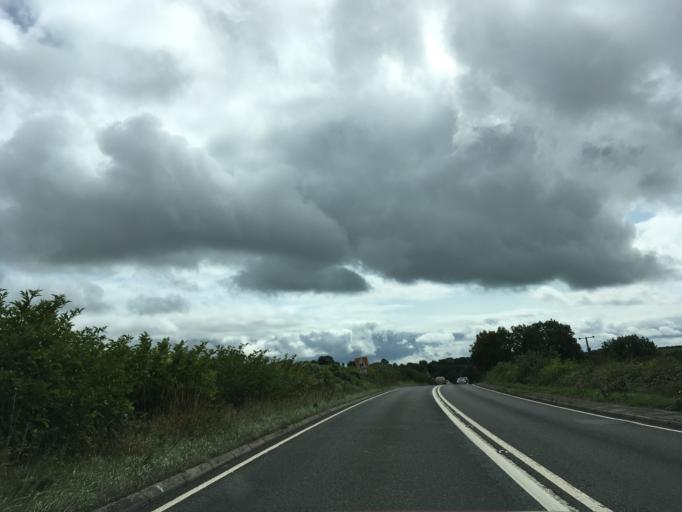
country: GB
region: England
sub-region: South Gloucestershire
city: Cold Ashton
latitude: 51.4485
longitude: -2.3660
